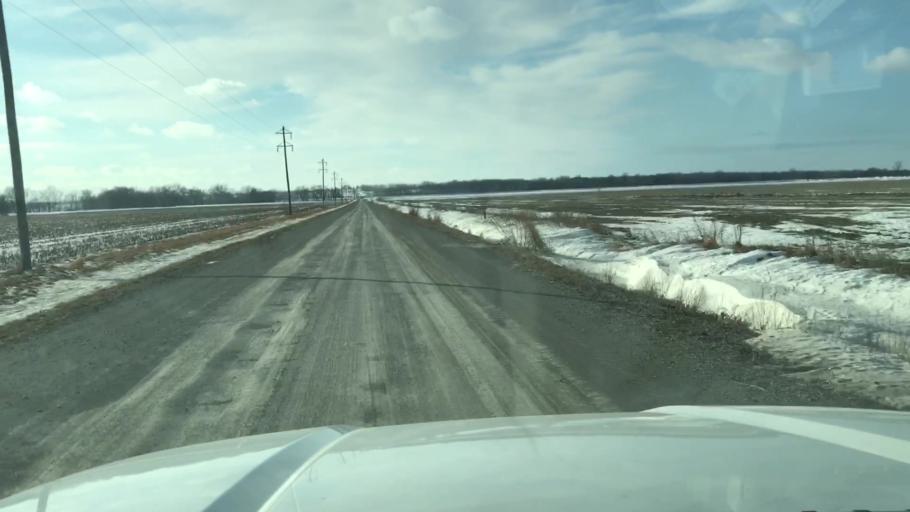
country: US
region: Missouri
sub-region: Holt County
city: Oregon
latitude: 40.1300
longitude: -95.0292
